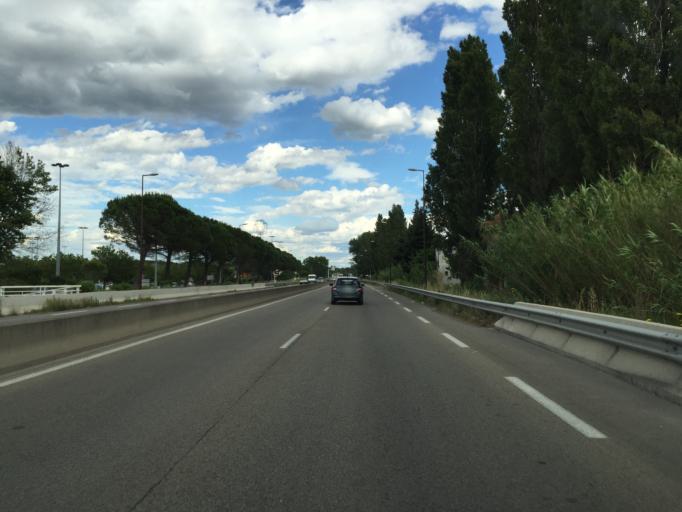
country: FR
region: Provence-Alpes-Cote d'Azur
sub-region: Departement du Vaucluse
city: Montfavet
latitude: 43.9206
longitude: 4.8618
